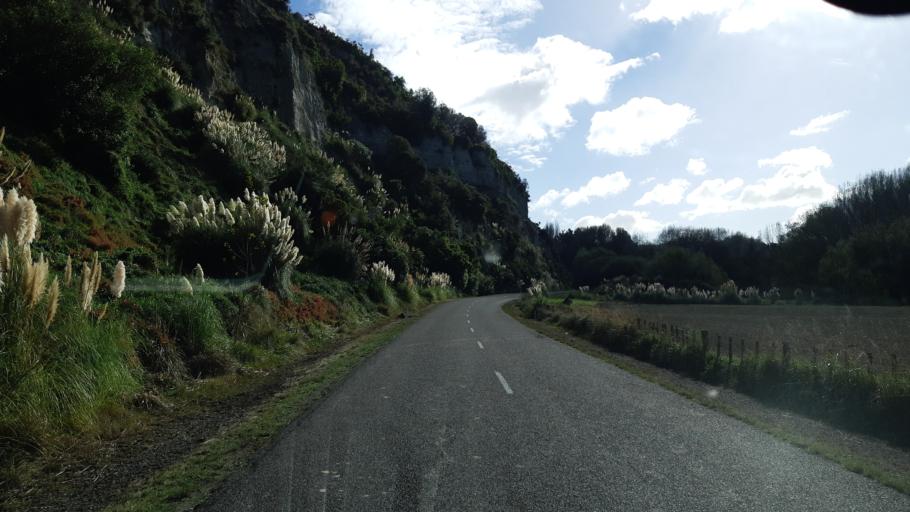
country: NZ
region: Manawatu-Wanganui
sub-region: Wanganui District
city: Wanganui
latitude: -39.9263
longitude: 175.2924
